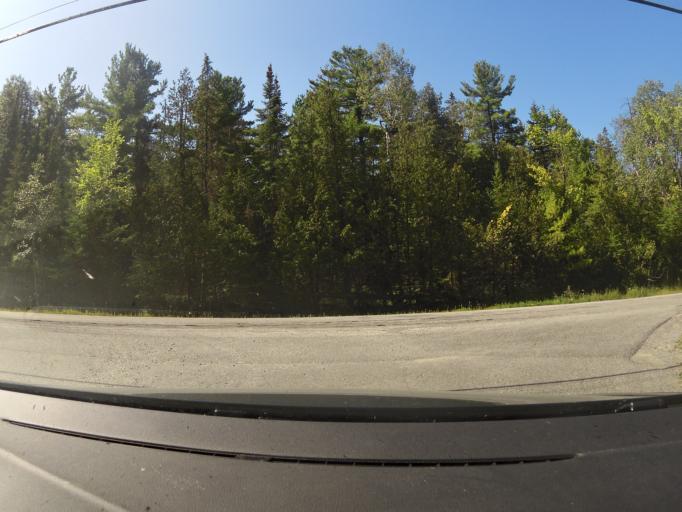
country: CA
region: Ontario
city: Bells Corners
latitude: 45.2705
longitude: -76.0129
